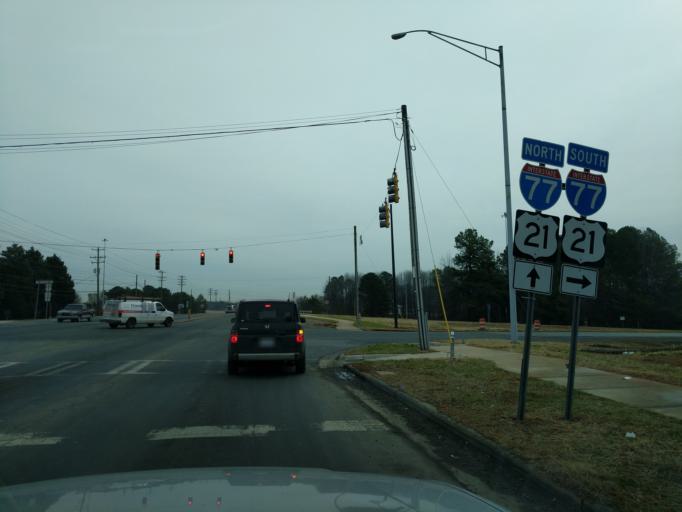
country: US
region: North Carolina
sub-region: Mecklenburg County
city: Charlotte
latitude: 35.3069
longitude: -80.8509
